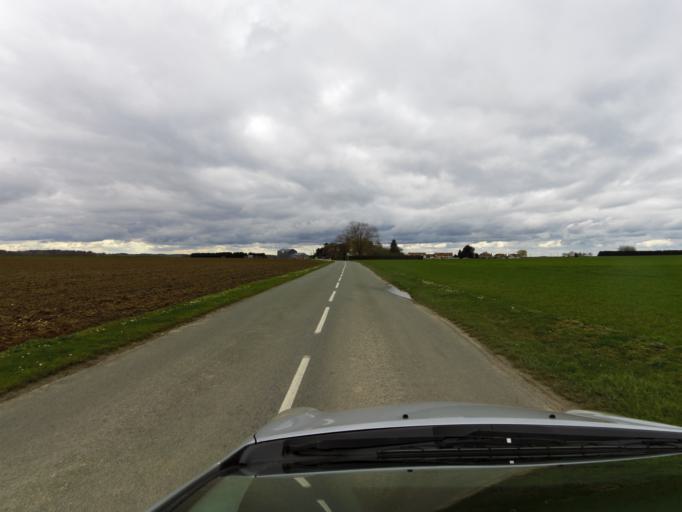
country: FR
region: Picardie
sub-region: Departement de la Somme
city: Bray-sur-Somme
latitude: 49.9055
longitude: 2.7987
